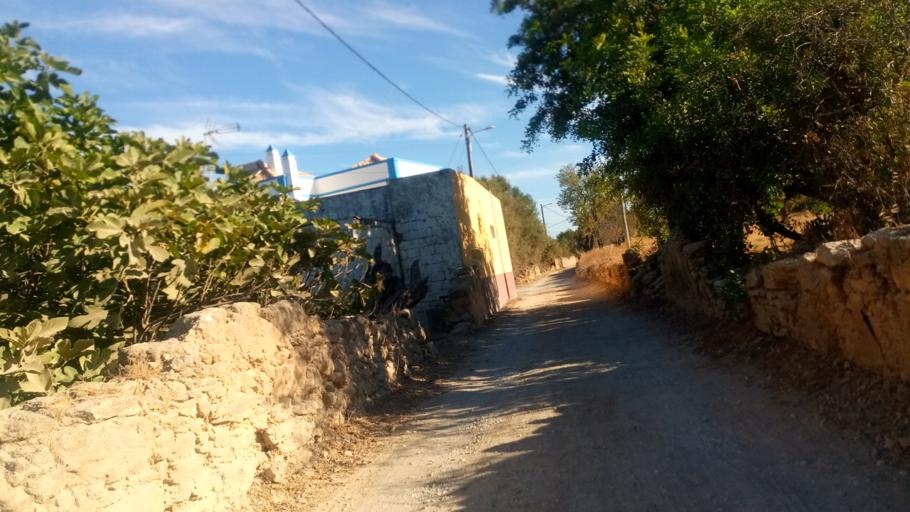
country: PT
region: Faro
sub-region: Tavira
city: Tavira
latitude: 37.1412
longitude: -7.5943
